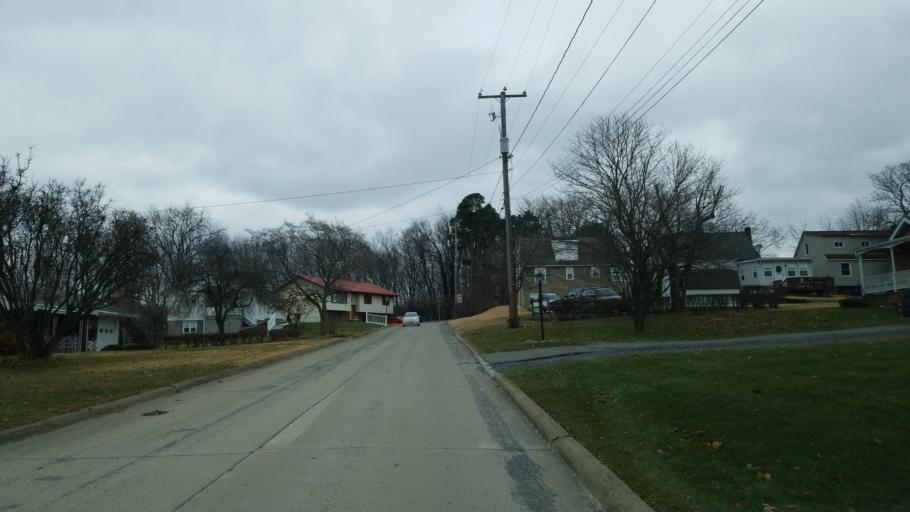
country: US
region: Pennsylvania
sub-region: Clearfield County
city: DuBois
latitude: 41.1307
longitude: -78.7646
